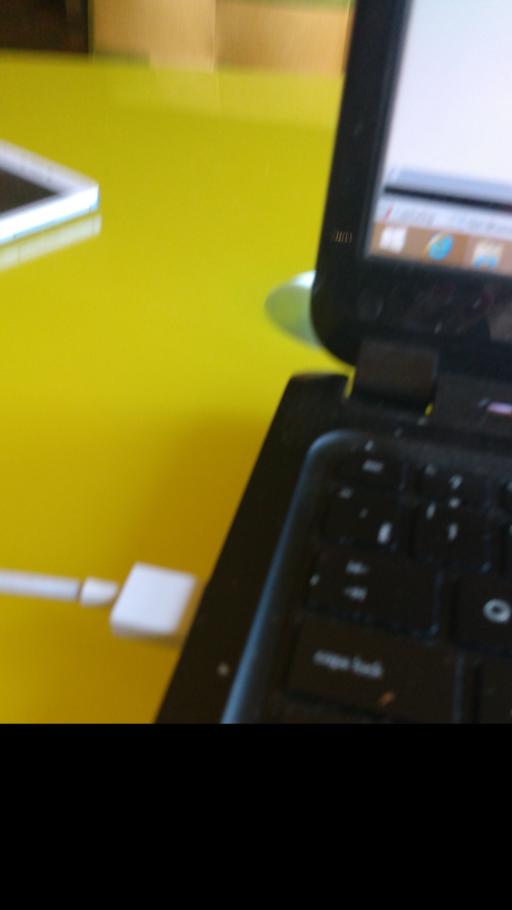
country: RU
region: Tverskaya
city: Gorodnya
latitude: 56.6942
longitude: 36.3210
